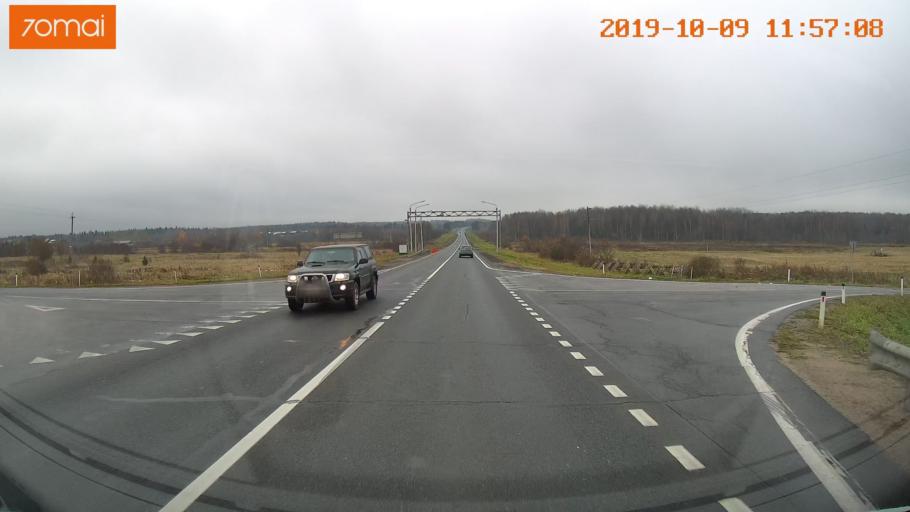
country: RU
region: Vologda
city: Gryazovets
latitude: 58.7362
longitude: 40.2909
